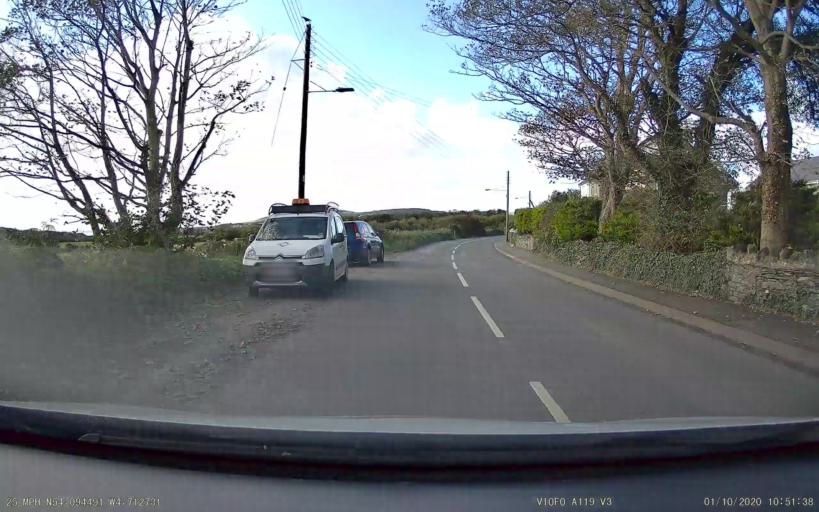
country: IM
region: Port Erin
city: Port Erin
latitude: 54.0945
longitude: -4.7127
